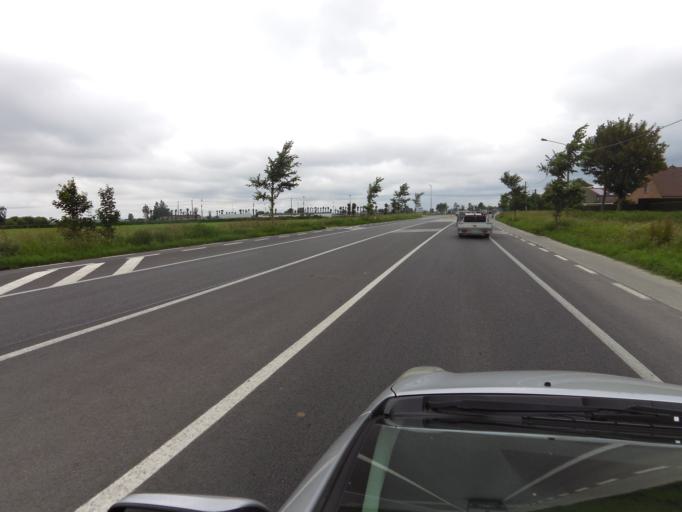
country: BE
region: Flanders
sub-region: Provincie West-Vlaanderen
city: Diksmuide
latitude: 51.0812
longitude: 2.8769
